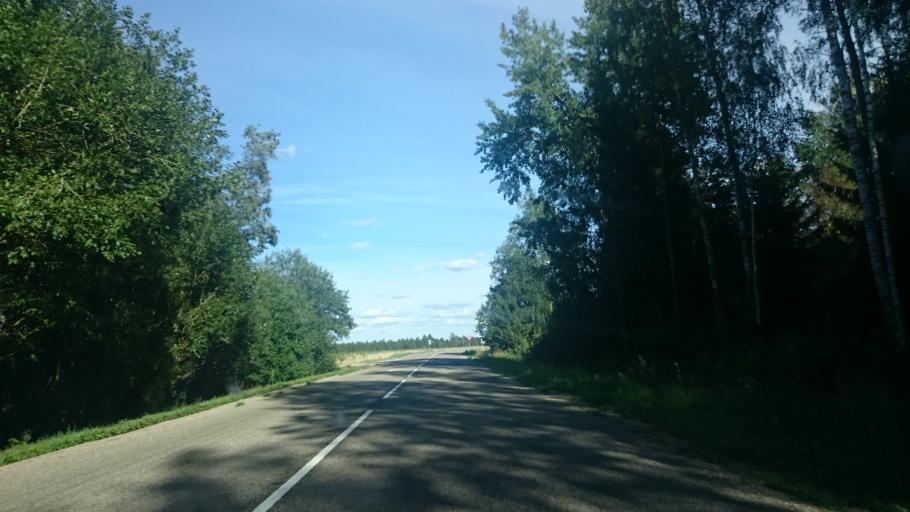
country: LV
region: Skrunda
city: Skrunda
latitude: 56.6816
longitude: 21.9143
